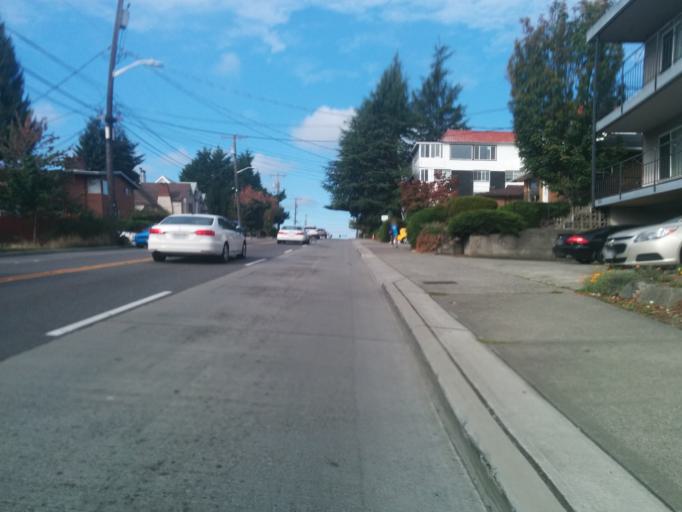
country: US
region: Washington
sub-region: King County
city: Shoreline
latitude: 47.6907
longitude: -122.3472
